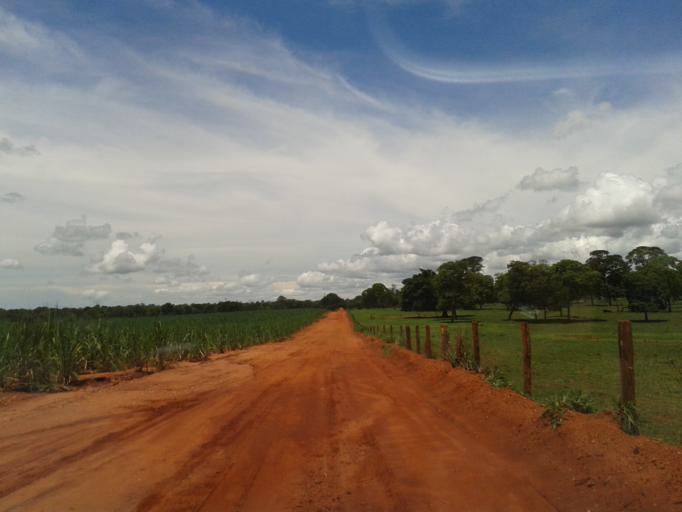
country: BR
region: Minas Gerais
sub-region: Santa Vitoria
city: Santa Vitoria
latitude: -19.1995
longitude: -50.6493
